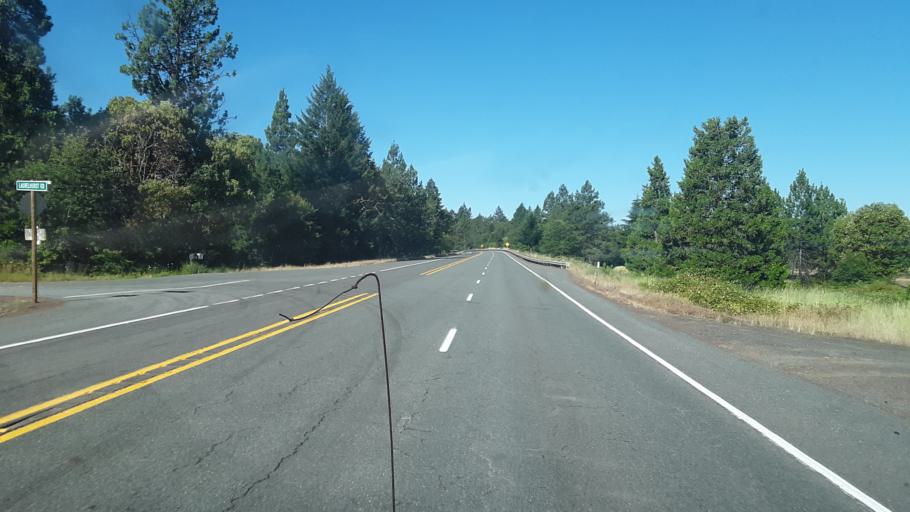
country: US
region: Oregon
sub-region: Jackson County
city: Shady Cove
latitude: 42.6881
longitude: -122.6048
